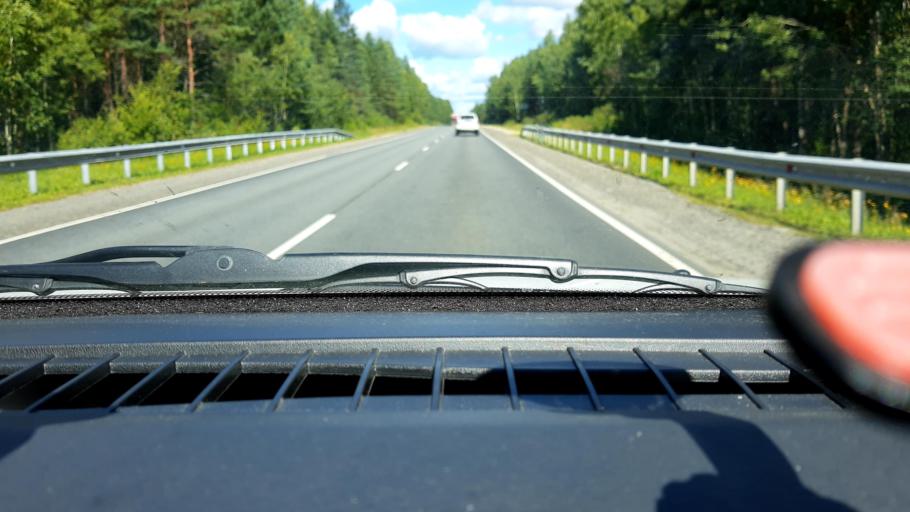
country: RU
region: Nizjnij Novgorod
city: Arzamas
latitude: 55.4405
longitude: 43.8924
